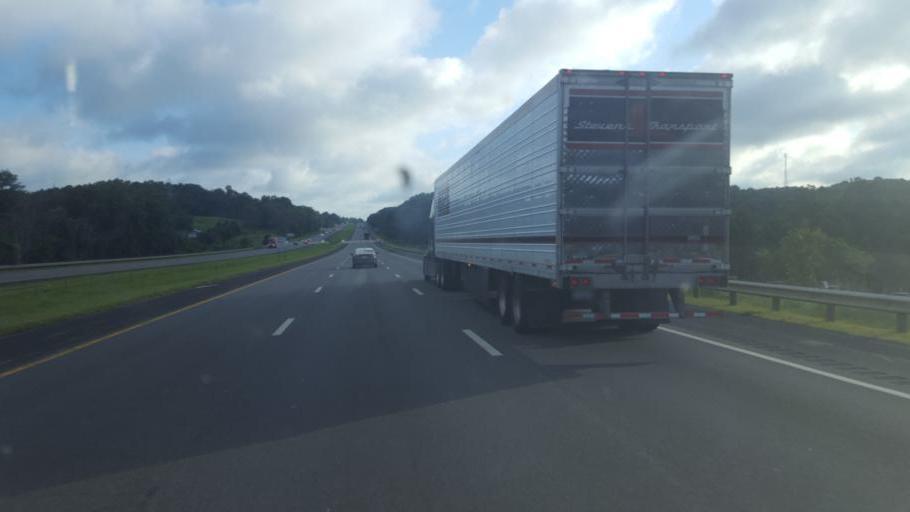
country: US
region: Ohio
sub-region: Richland County
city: Lexington
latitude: 40.6684
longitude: -82.5346
